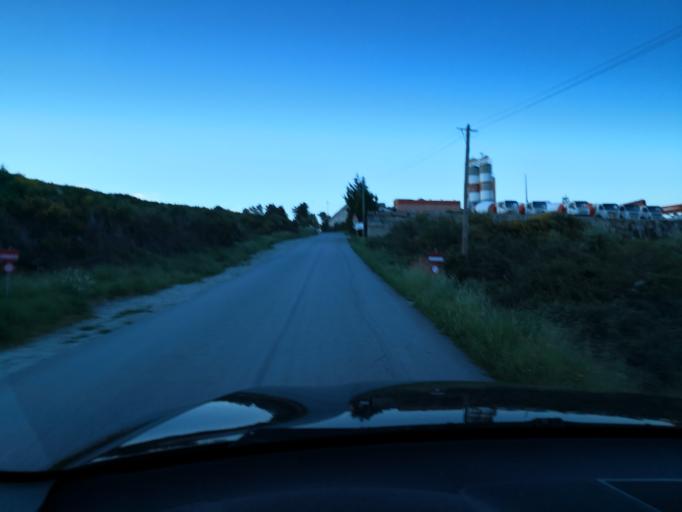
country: PT
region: Vila Real
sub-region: Vila Real
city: Vila Real
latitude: 41.3425
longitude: -7.6956
